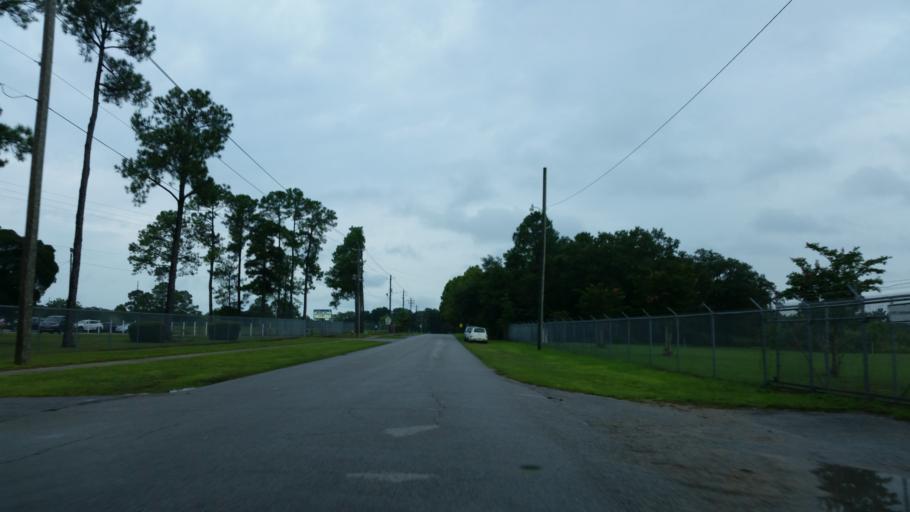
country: US
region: Florida
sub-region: Escambia County
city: West Pensacola
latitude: 30.4358
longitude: -87.2591
